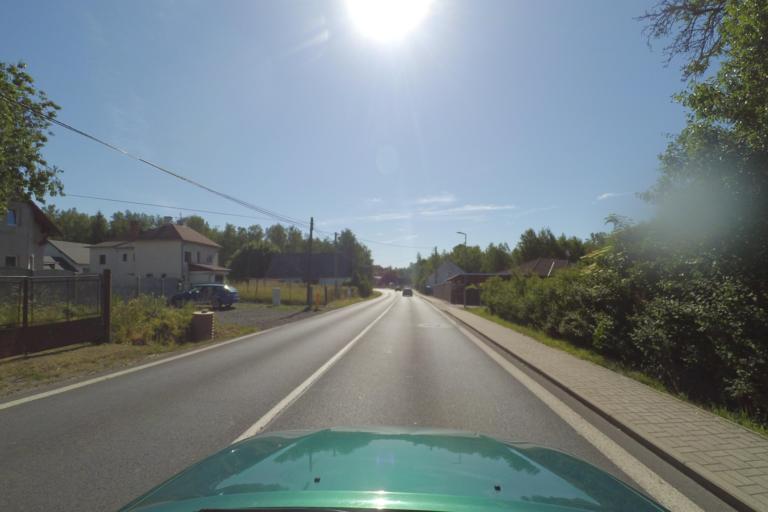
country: CZ
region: Karlovarsky
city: Chodov
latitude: 50.2382
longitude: 12.7660
